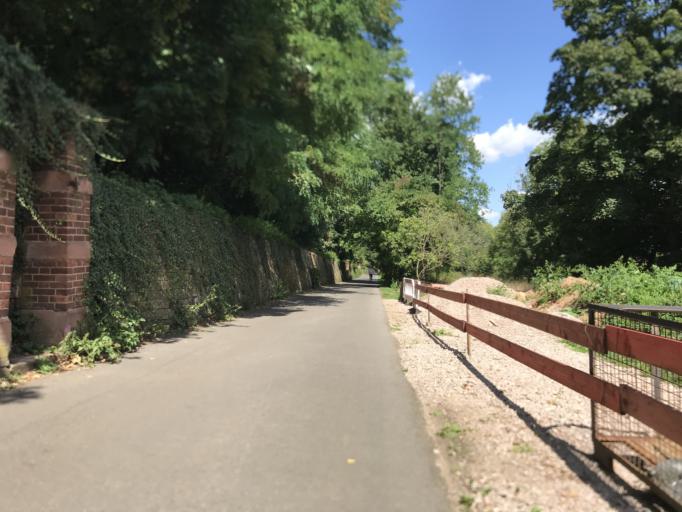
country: DE
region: Rheinland-Pfalz
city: Bad Kreuznach
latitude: 49.8341
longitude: 7.8487
